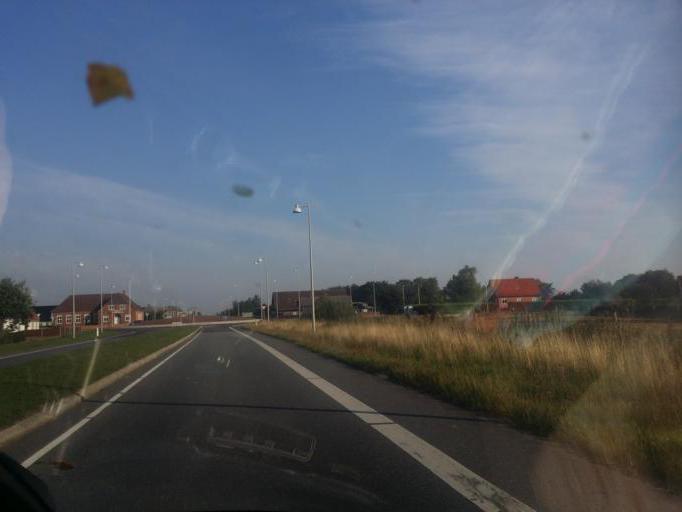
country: DK
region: South Denmark
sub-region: Tonder Kommune
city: Tonder
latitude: 55.0135
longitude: 8.8477
